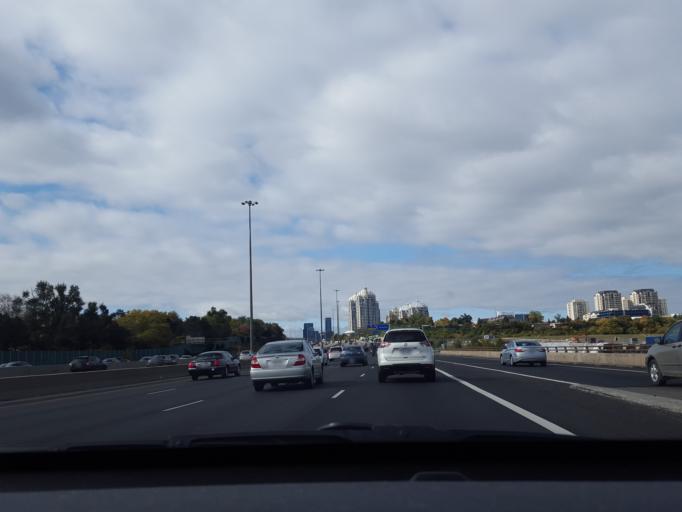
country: CA
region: Ontario
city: Willowdale
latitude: 43.7664
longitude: -79.3675
